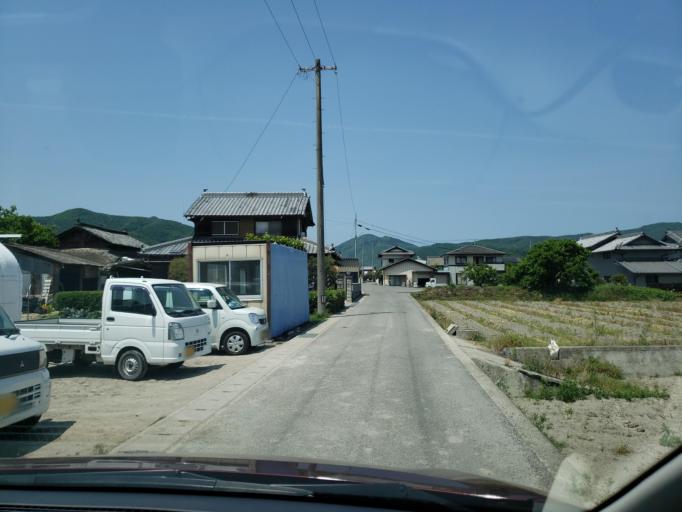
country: JP
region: Tokushima
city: Kamojimacho-jogejima
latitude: 34.0899
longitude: 134.2681
